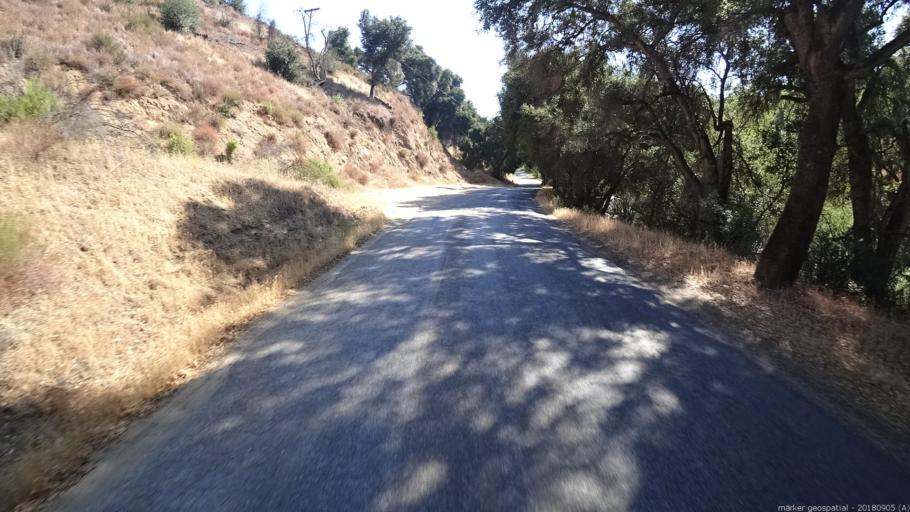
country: US
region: California
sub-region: Monterey County
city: Gonzales
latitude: 36.3940
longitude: -121.5853
